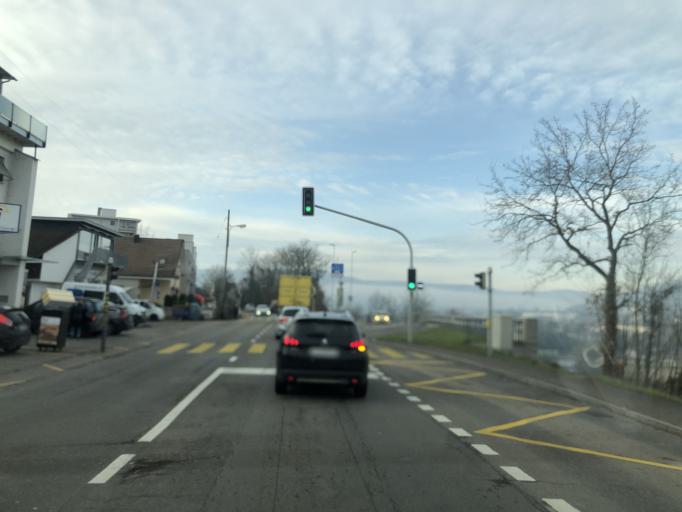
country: CH
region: Aargau
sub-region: Bezirk Baden
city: Turgi
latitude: 47.4885
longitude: 8.2615
